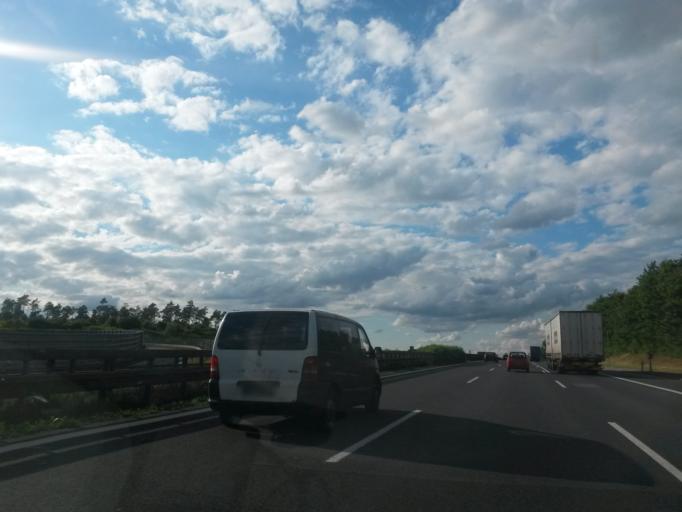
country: DE
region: Bavaria
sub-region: Regierungsbezirk Mittelfranken
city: Allersberg
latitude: 49.2508
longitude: 11.2161
